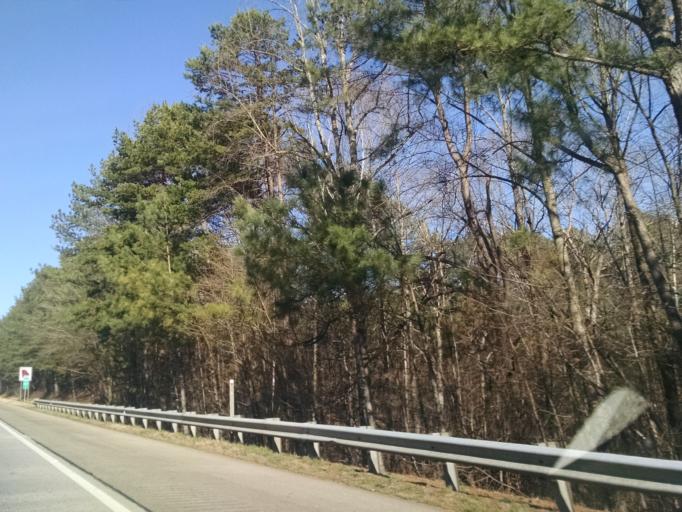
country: US
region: Georgia
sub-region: Gwinnett County
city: Suwanee
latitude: 34.0551
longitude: -84.0239
